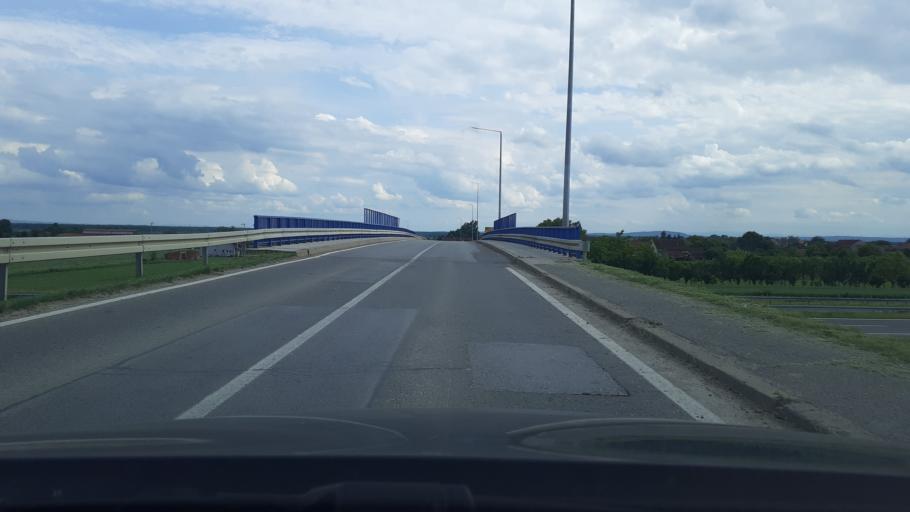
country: HR
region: Brodsko-Posavska
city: Slobodnica
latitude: 45.1702
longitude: 17.9309
